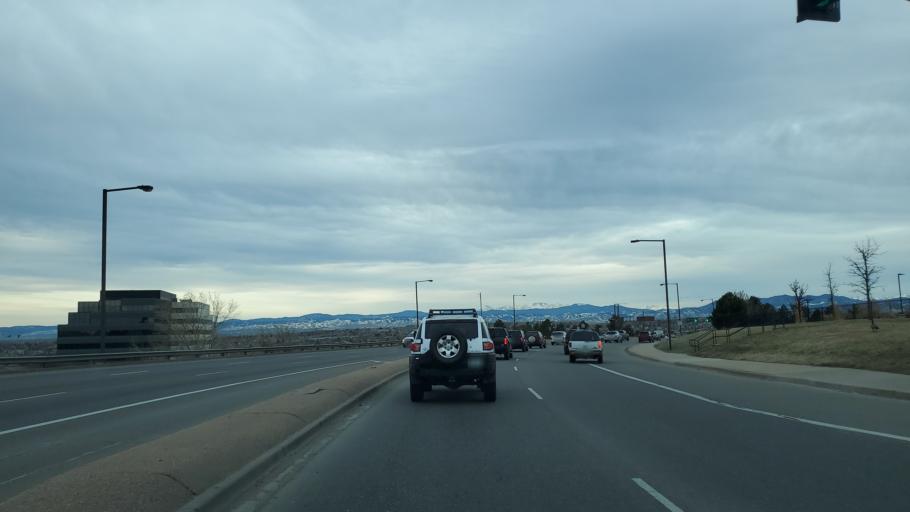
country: US
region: Colorado
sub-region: Adams County
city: Thornton
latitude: 39.8689
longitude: -104.9844
